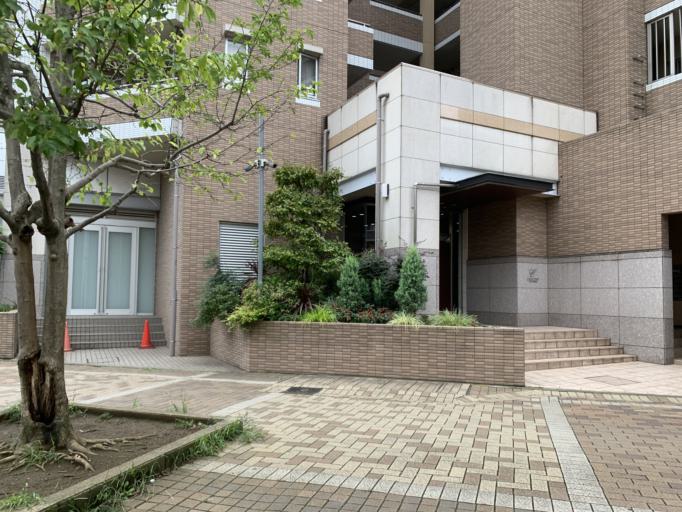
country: JP
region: Kanagawa
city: Yokohama
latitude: 35.5363
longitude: 139.5892
